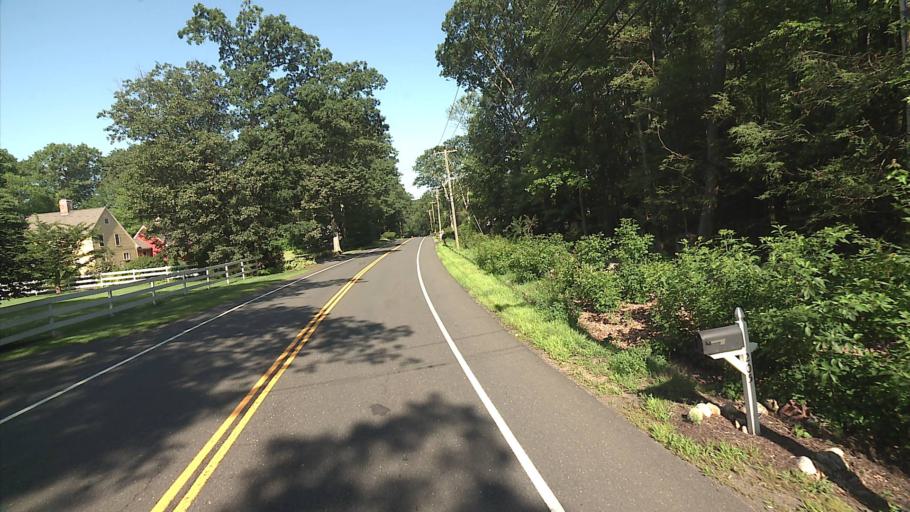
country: US
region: Connecticut
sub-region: Hartford County
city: Salmon Brook
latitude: 41.9551
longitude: -72.8288
